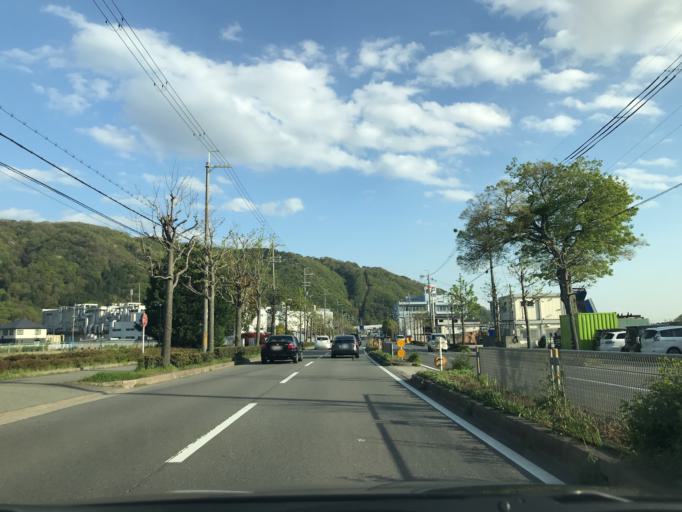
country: JP
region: Osaka
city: Ikeda
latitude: 34.8451
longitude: 135.4228
